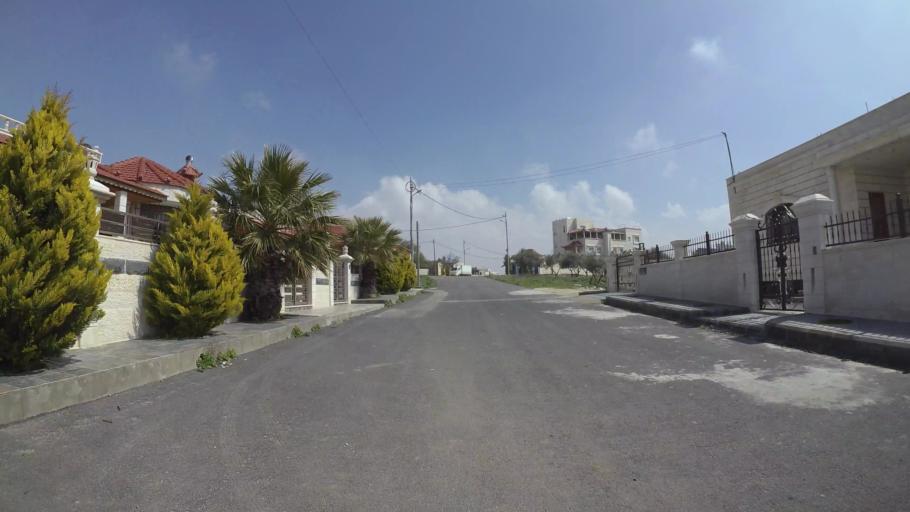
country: JO
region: Amman
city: Al Bunayyat ash Shamaliyah
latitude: 31.8935
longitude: 35.8913
